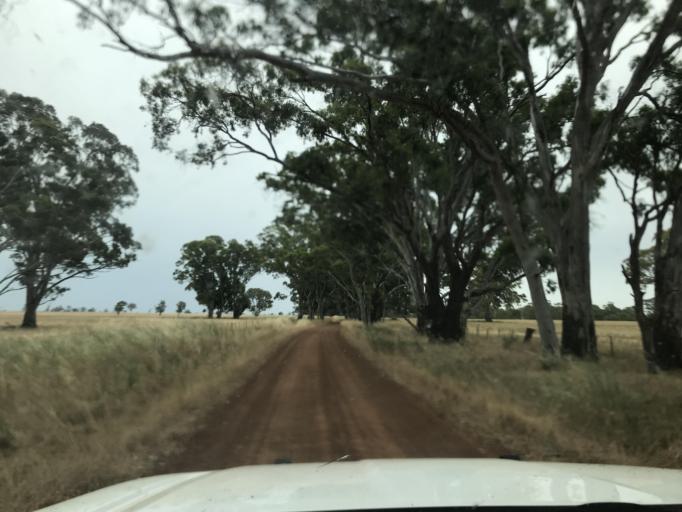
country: AU
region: Victoria
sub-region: Horsham
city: Horsham
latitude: -37.0655
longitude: 141.6612
